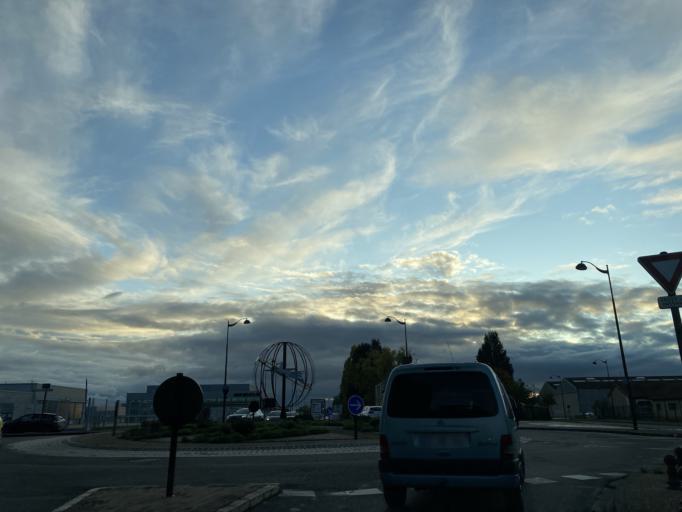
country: FR
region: Centre
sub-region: Departement du Cher
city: Bourges
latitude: 47.0688
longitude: 2.3746
